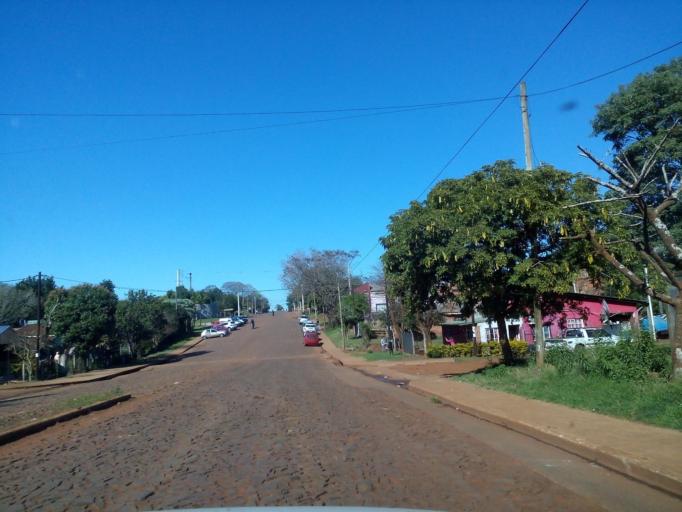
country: AR
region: Misiones
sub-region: Departamento de Capital
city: Posadas
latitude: -27.3778
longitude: -55.9484
